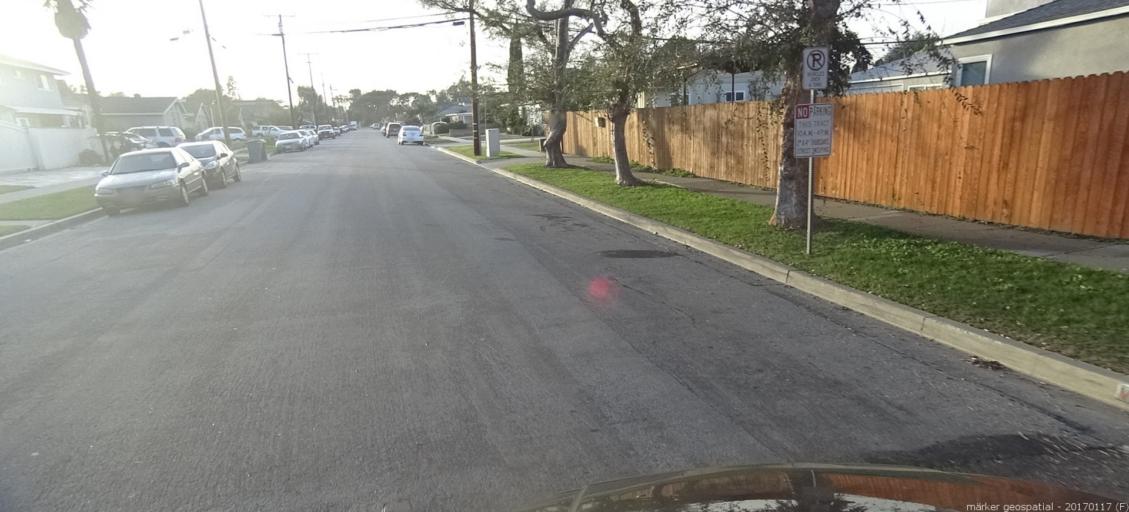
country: US
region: California
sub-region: Orange County
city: Midway City
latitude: 33.7511
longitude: -117.9854
